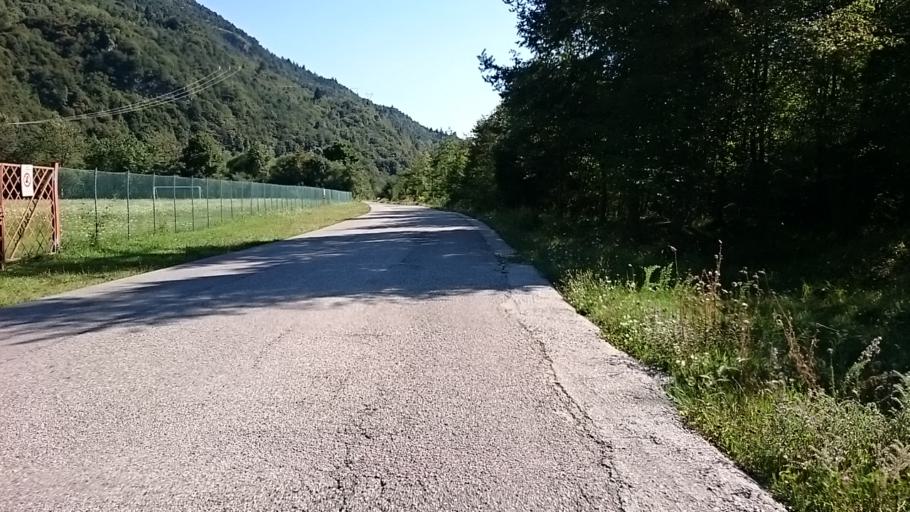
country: IT
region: Veneto
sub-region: Provincia di Belluno
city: Longarone
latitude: 46.2401
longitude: 12.3076
